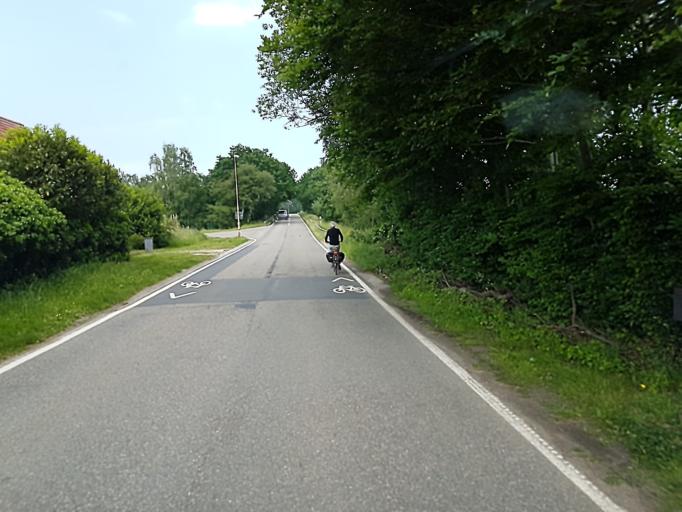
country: BE
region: Flanders
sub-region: Provincie Antwerpen
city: Ranst
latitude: 51.2055
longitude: 4.5520
